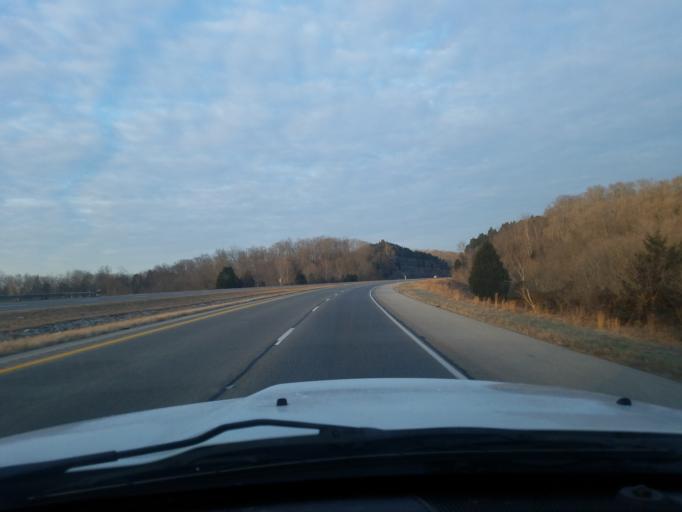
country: US
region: Indiana
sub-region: Harrison County
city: Corydon
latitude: 38.2348
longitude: -86.2342
